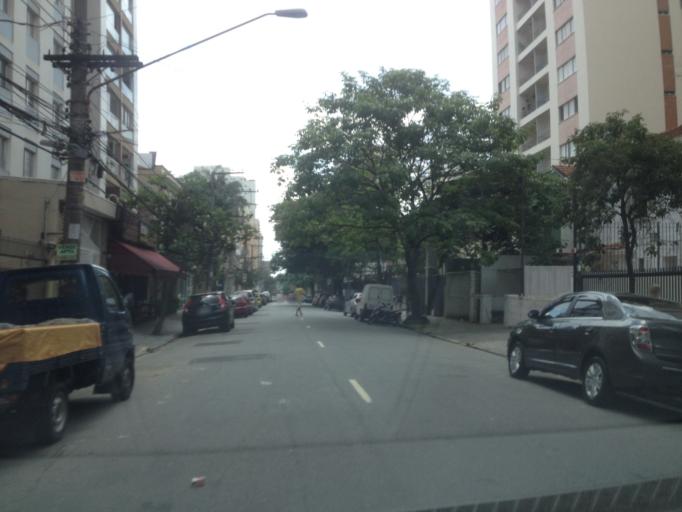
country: BR
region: Sao Paulo
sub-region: Sao Paulo
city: Sao Paulo
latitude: -23.5612
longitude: -46.6825
